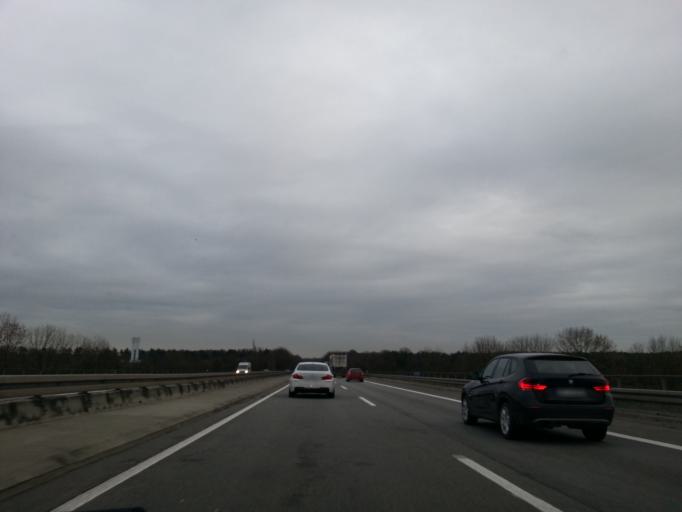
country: DE
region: North Rhine-Westphalia
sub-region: Regierungsbezirk Dusseldorf
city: Hunxe
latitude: 51.6471
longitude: 6.7391
